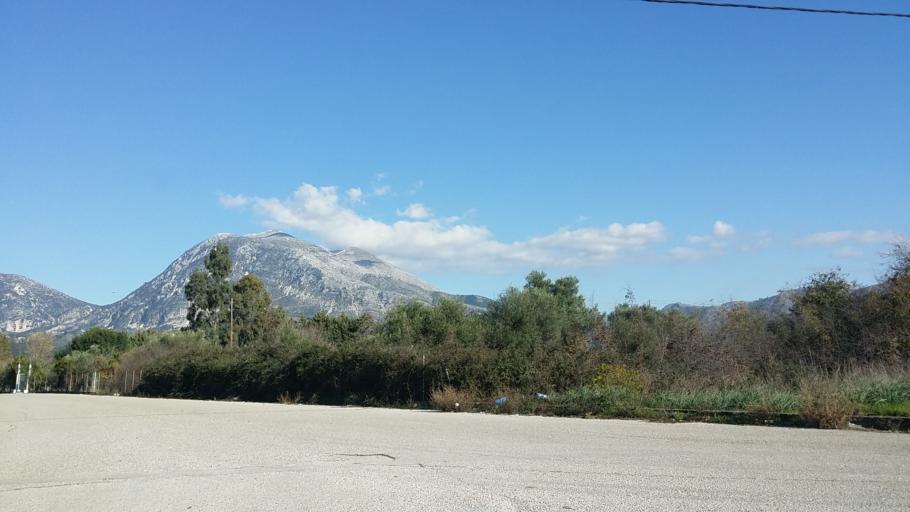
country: GR
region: West Greece
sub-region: Nomos Aitolias kai Akarnanias
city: Kandila
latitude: 38.6734
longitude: 20.9494
